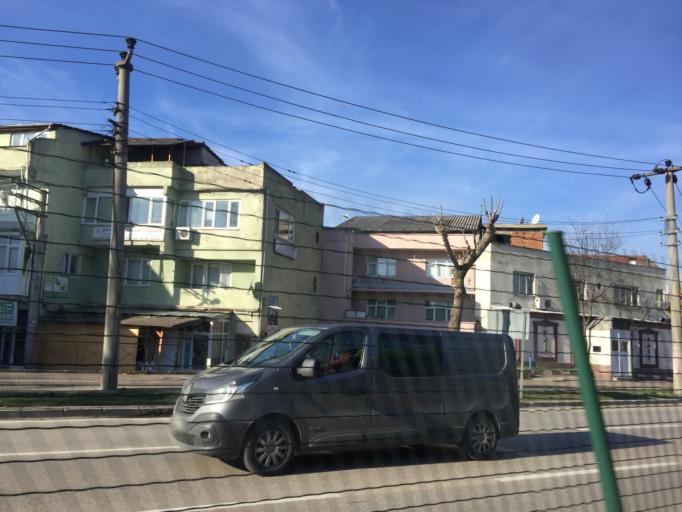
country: TR
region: Bursa
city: Yildirim
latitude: 40.2222
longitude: 28.9948
